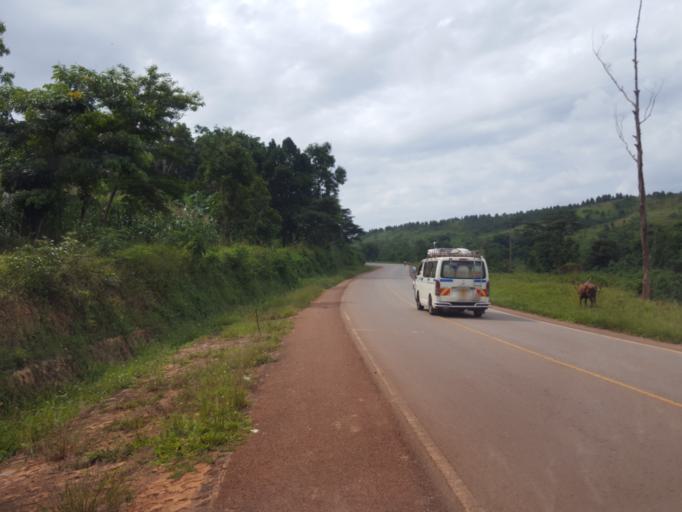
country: UG
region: Central Region
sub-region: Mityana District
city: Mityana
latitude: 0.6270
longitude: 32.1182
